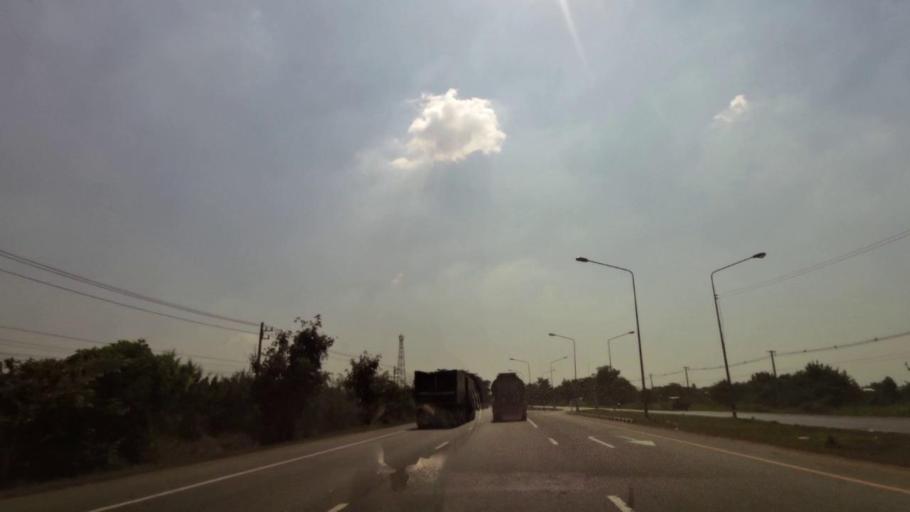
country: TH
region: Phichit
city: Bueng Na Rang
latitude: 16.1622
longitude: 100.1260
